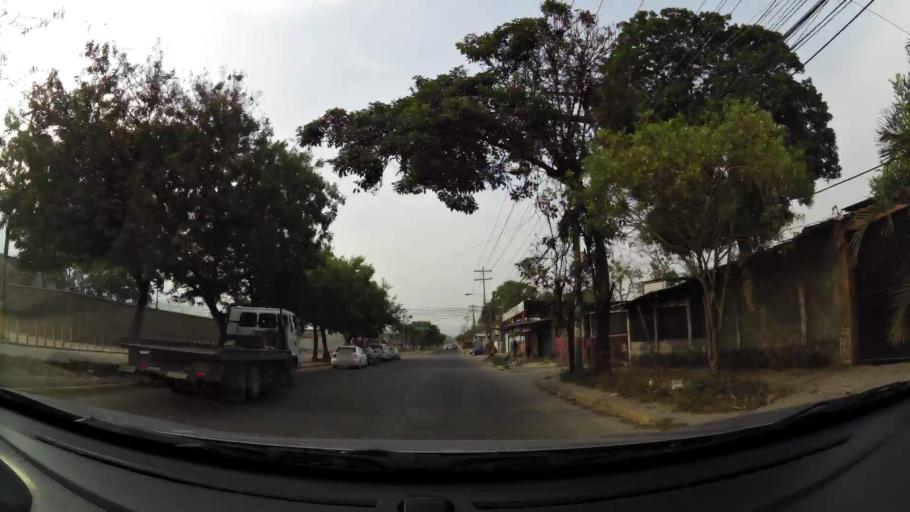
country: HN
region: Cortes
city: San Pedro Sula
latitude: 15.5279
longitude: -88.0150
